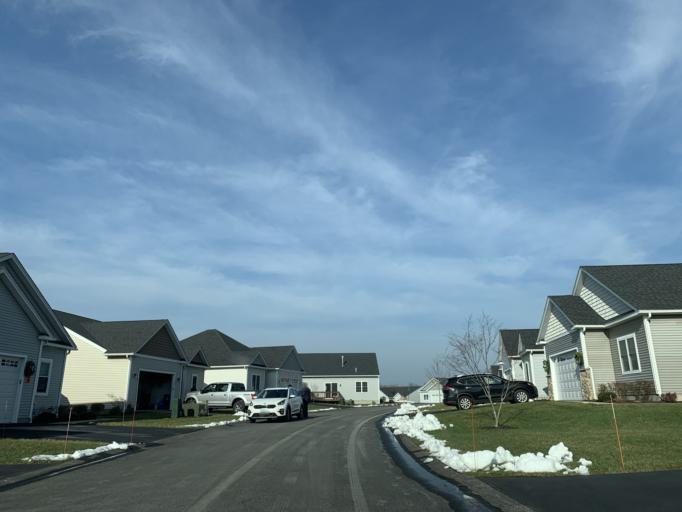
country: US
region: Rhode Island
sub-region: Kent County
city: West Warwick
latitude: 41.6559
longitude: -71.5474
